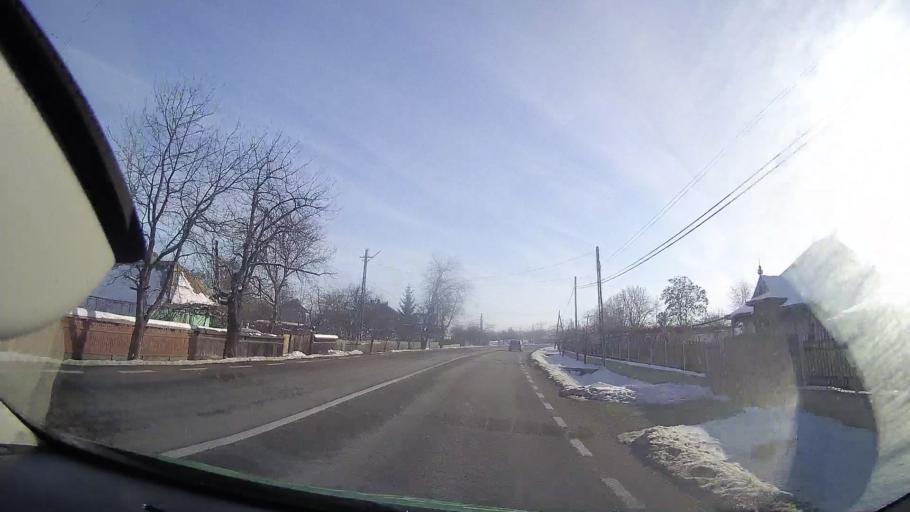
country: RO
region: Neamt
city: Bodesti
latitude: 47.0521
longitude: 26.4018
